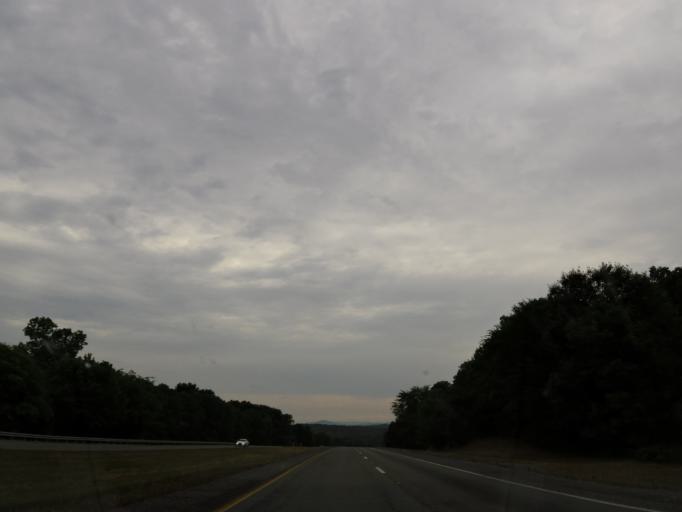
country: US
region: Alabama
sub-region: Jackson County
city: Scottsboro
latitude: 34.6169
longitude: -86.2157
